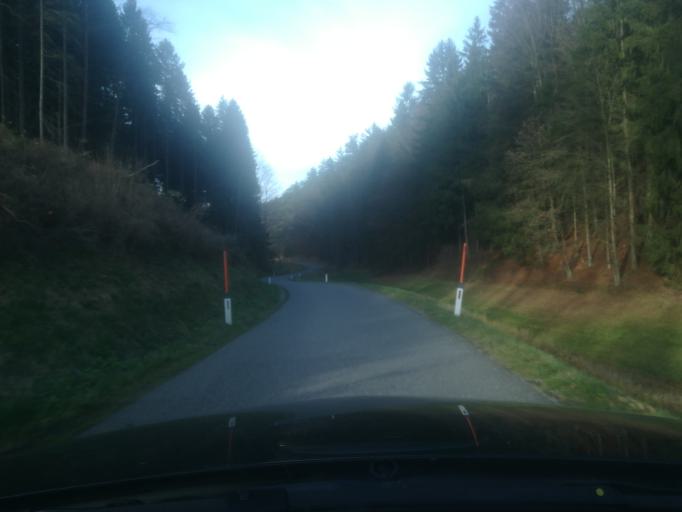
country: AT
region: Upper Austria
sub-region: Politischer Bezirk Perg
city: Perg
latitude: 48.3349
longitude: 14.6479
